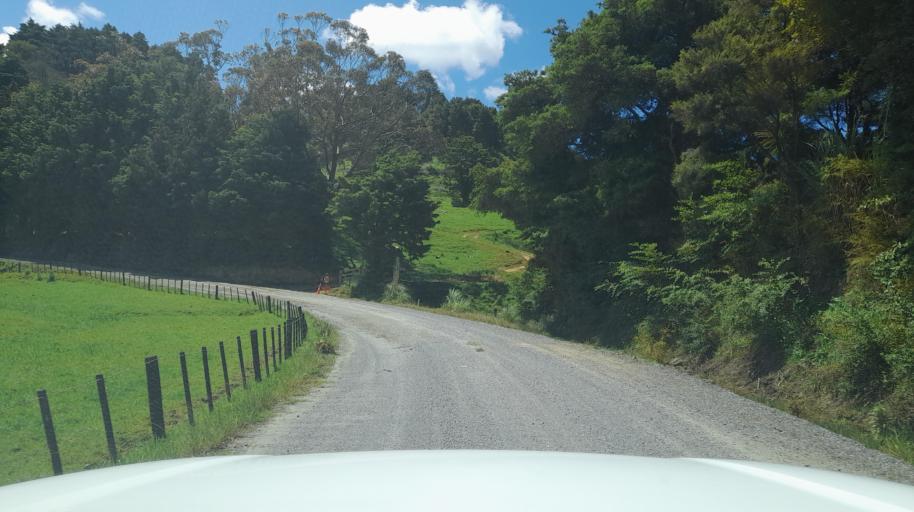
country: NZ
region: Northland
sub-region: Far North District
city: Kaitaia
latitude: -35.1089
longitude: 173.3952
